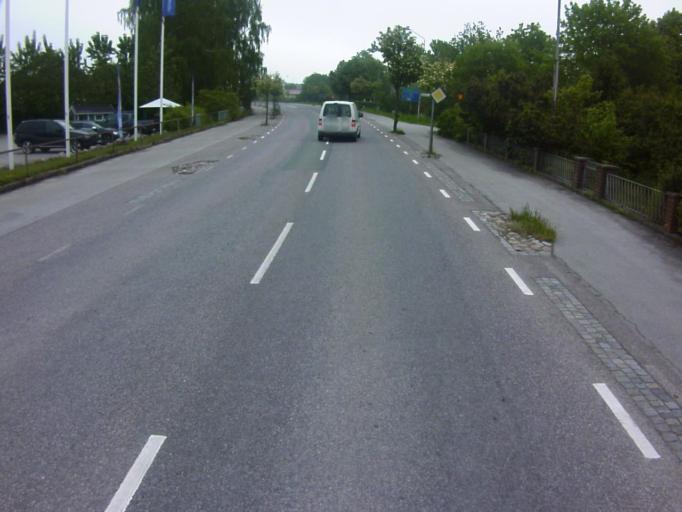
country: SE
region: Blekinge
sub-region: Solvesborgs Kommun
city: Soelvesborg
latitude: 56.0604
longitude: 14.6180
